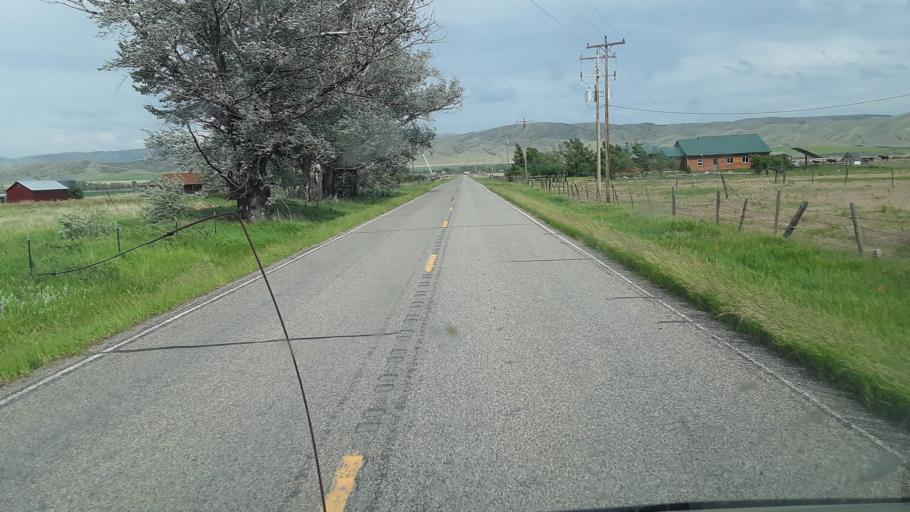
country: US
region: Montana
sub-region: Broadwater County
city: Townsend
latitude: 46.1736
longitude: -111.4651
